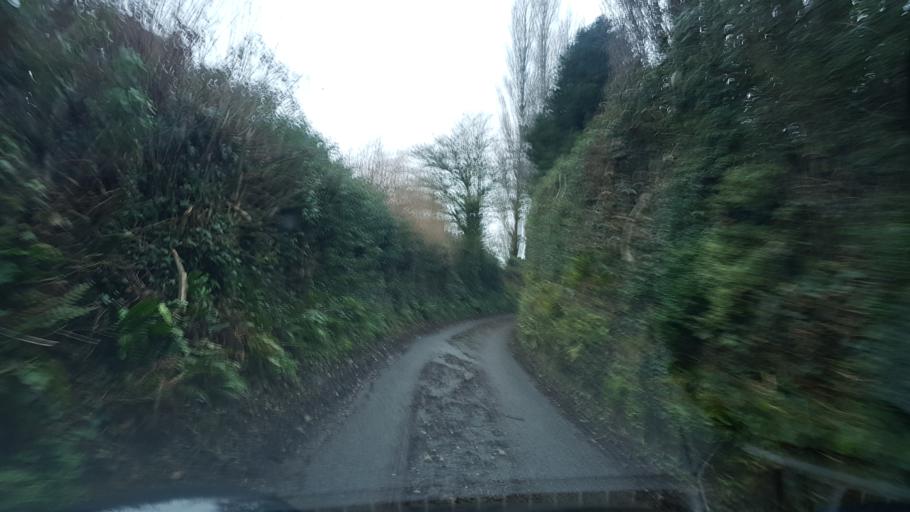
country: GB
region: England
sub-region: Somerset
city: Chard
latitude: 50.8965
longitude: -2.9701
